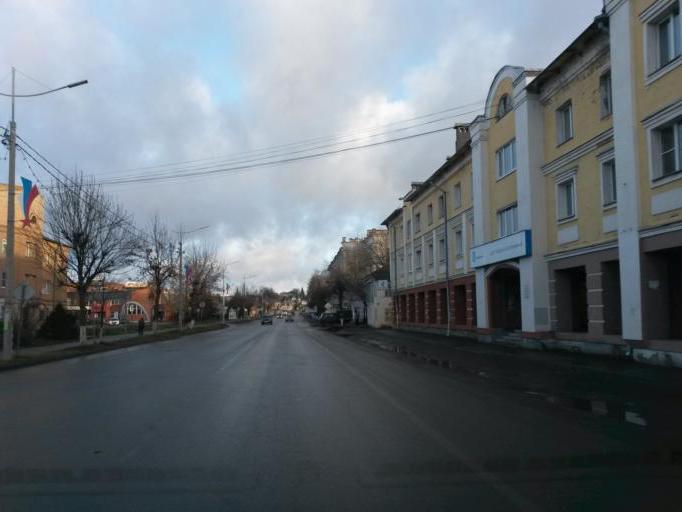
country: RU
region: Jaroslavl
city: Pereslavl'-Zalesskiy
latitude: 56.7414
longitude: 38.8564
